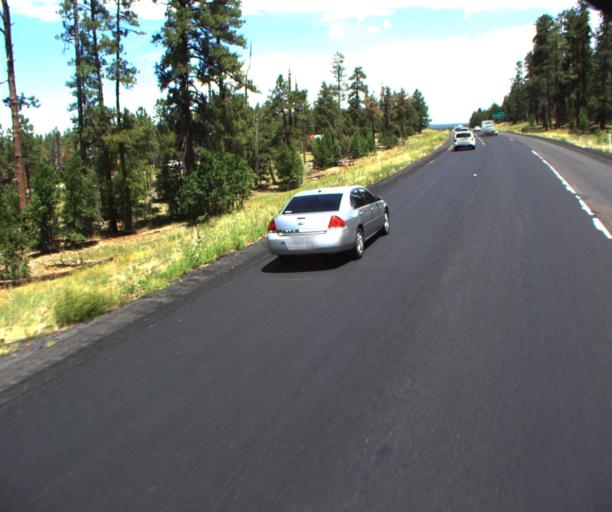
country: US
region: Arizona
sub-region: Coconino County
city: Sedona
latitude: 34.8333
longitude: -111.6051
